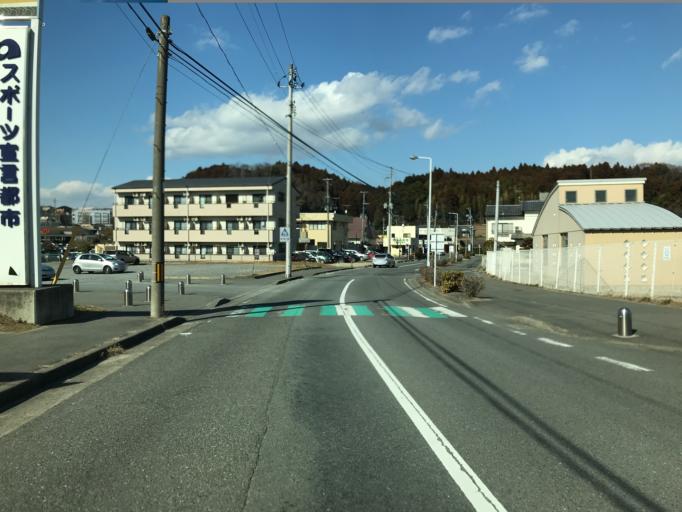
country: JP
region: Fukushima
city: Iwaki
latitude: 37.0361
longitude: 140.8949
